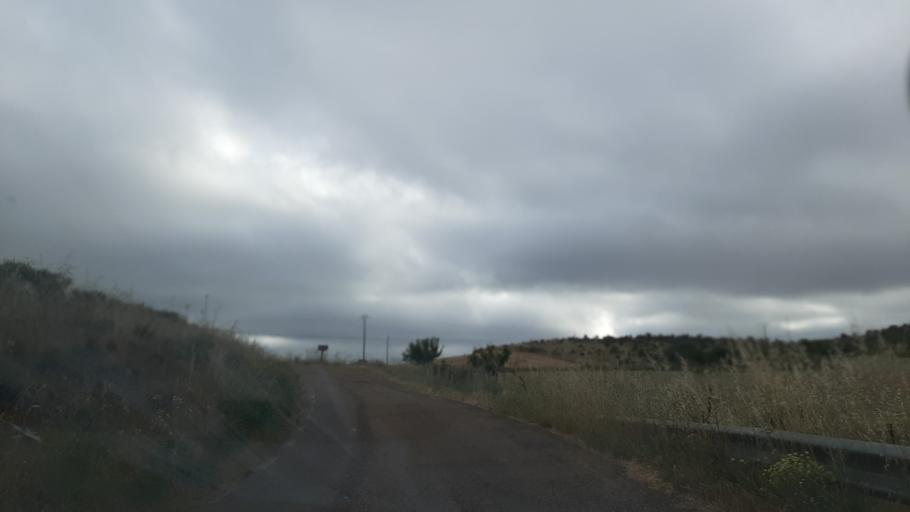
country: ES
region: Castille and Leon
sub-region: Provincia de Salamanca
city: Zamarra
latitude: 40.5275
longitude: -6.4675
